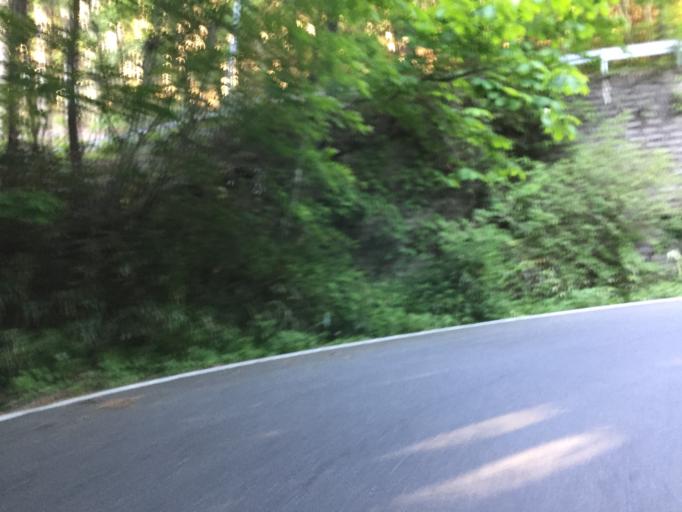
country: JP
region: Ibaraki
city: Kitaibaraki
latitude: 36.8964
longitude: 140.6201
